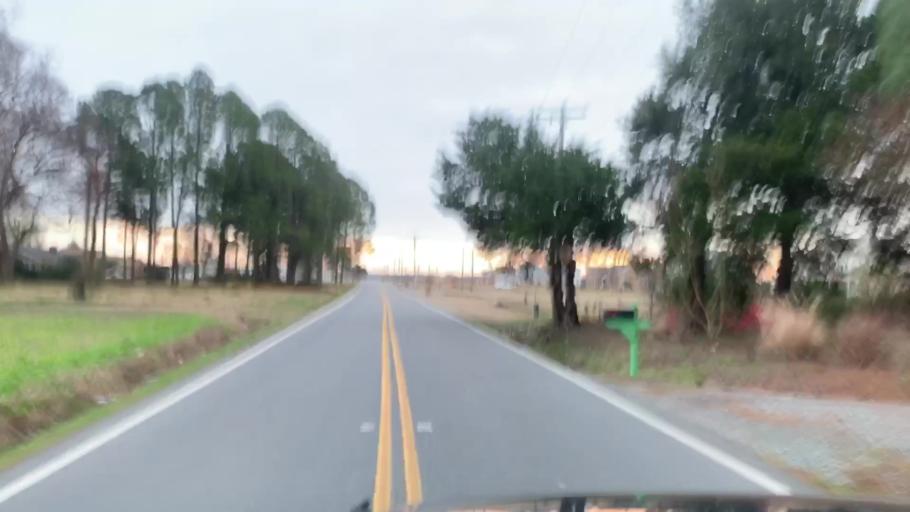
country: US
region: North Carolina
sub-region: Currituck County
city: Moyock
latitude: 36.6240
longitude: -76.1588
